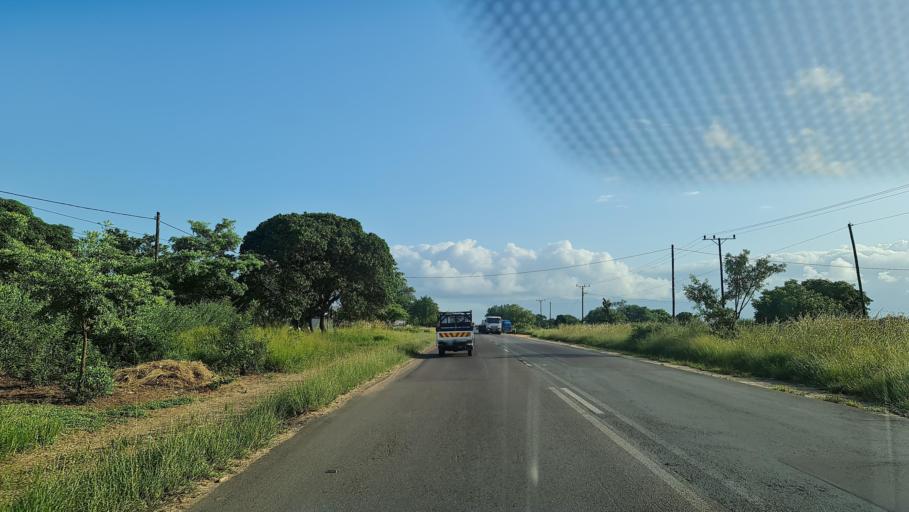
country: MZ
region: Maputo City
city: Maputo
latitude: -25.6884
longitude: 32.6646
